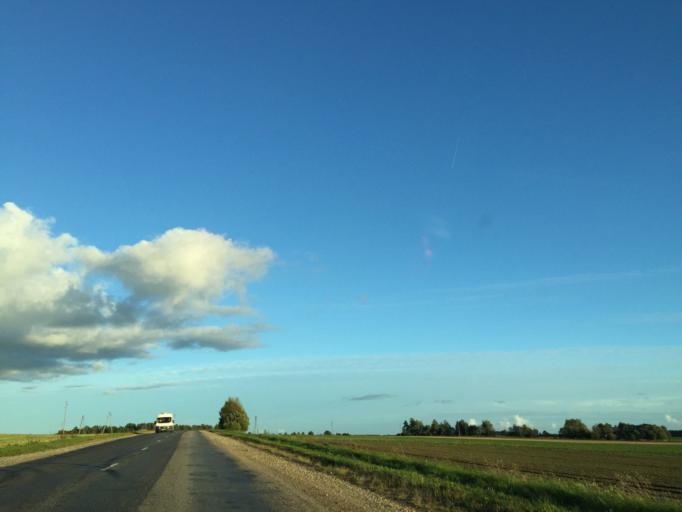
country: LV
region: Saldus Rajons
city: Saldus
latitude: 56.7073
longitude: 22.4215
